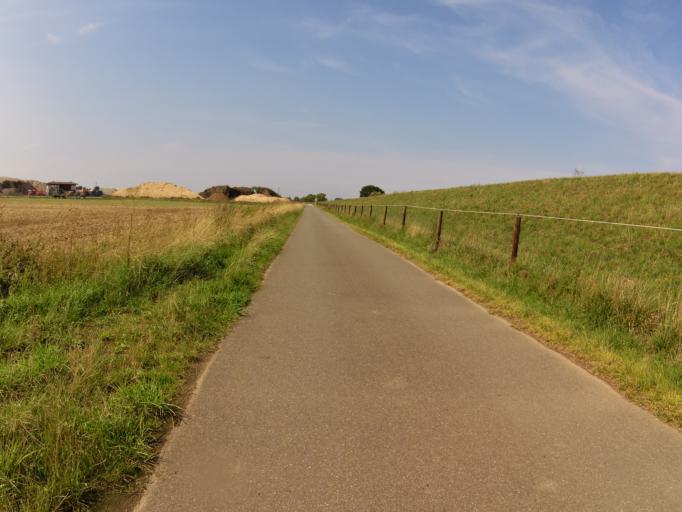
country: DE
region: Lower Saxony
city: Riede
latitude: 53.0034
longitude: 8.9069
